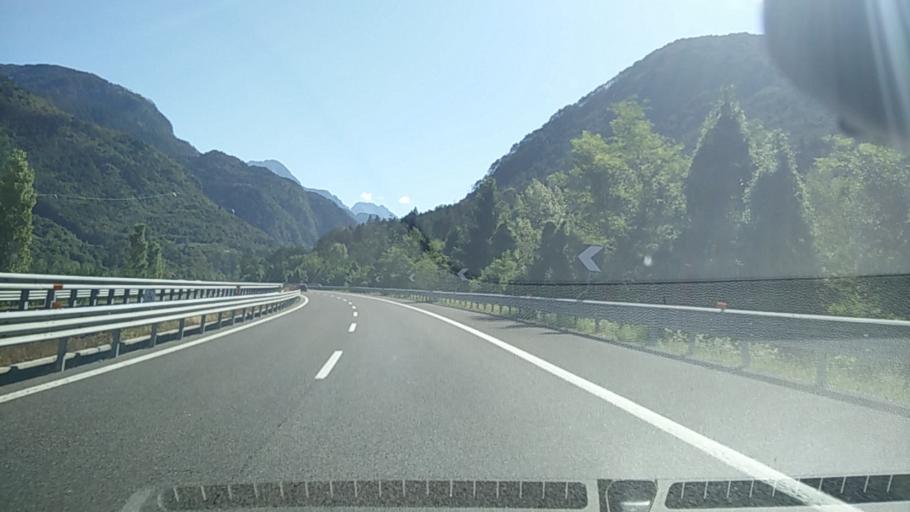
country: IT
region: Friuli Venezia Giulia
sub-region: Provincia di Udine
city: Resiutta
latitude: 46.3929
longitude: 13.2384
